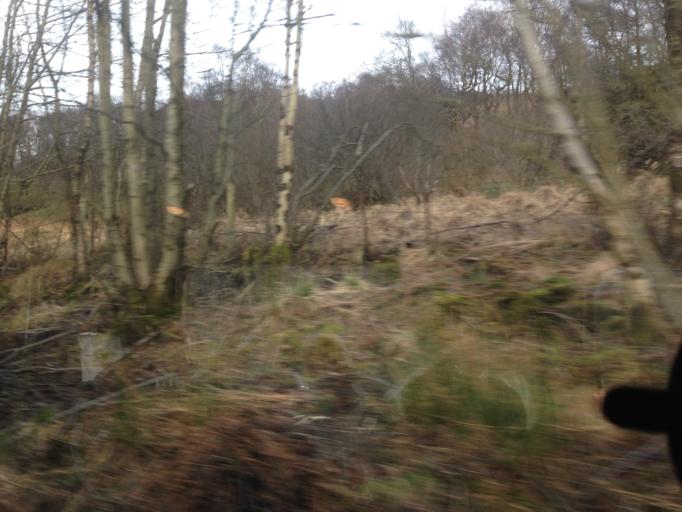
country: GB
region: Scotland
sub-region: Argyll and Bute
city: Garelochhead
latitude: 56.1681
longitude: -4.7811
